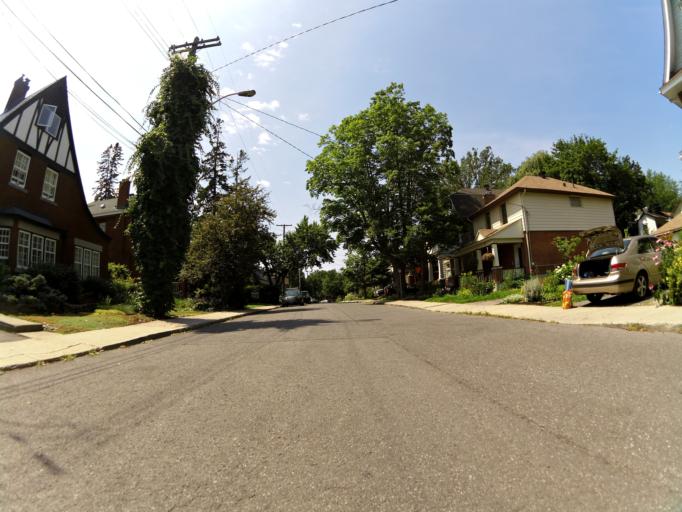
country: CA
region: Ontario
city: Ottawa
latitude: 45.3948
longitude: -75.6772
